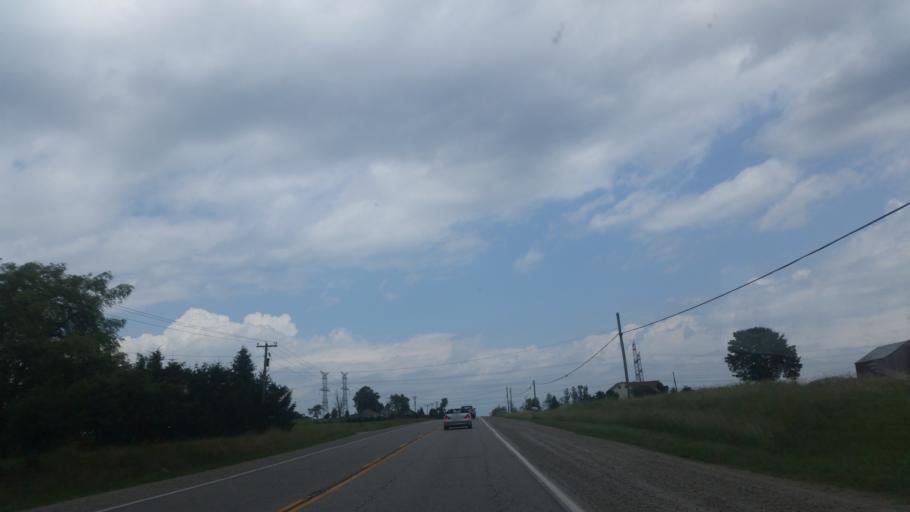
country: CA
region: Ontario
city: Orangeville
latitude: 43.7185
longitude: -80.1116
